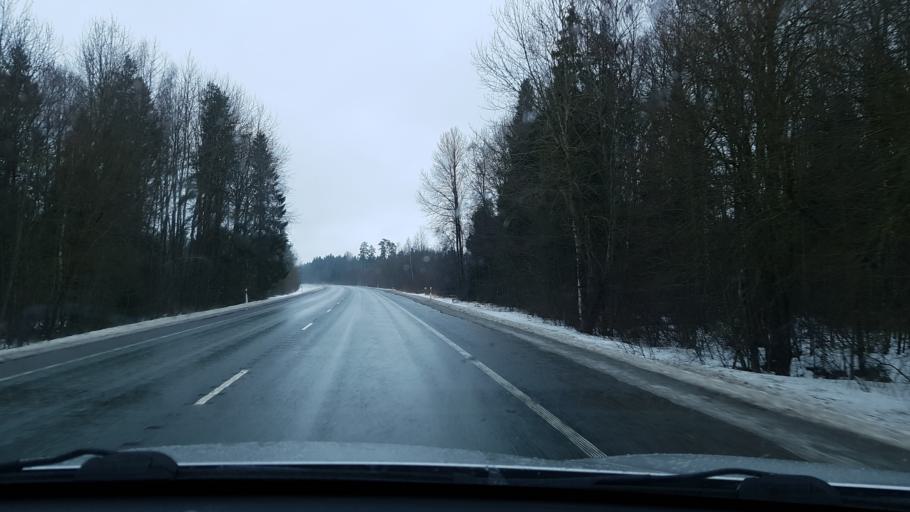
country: EE
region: Raplamaa
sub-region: Kohila vald
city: Kohila
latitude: 59.1394
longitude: 24.7908
